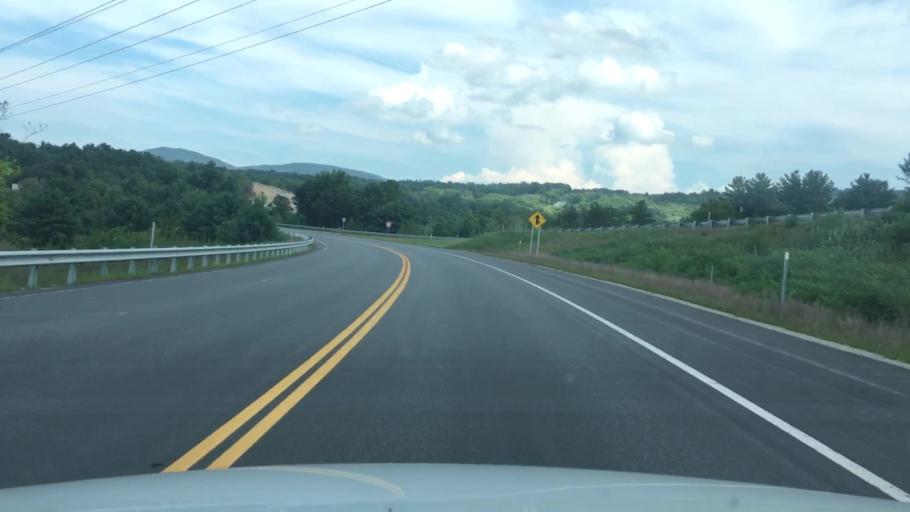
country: US
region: New Hampshire
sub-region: Belknap County
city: Laconia
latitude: 43.5122
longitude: -71.4583
